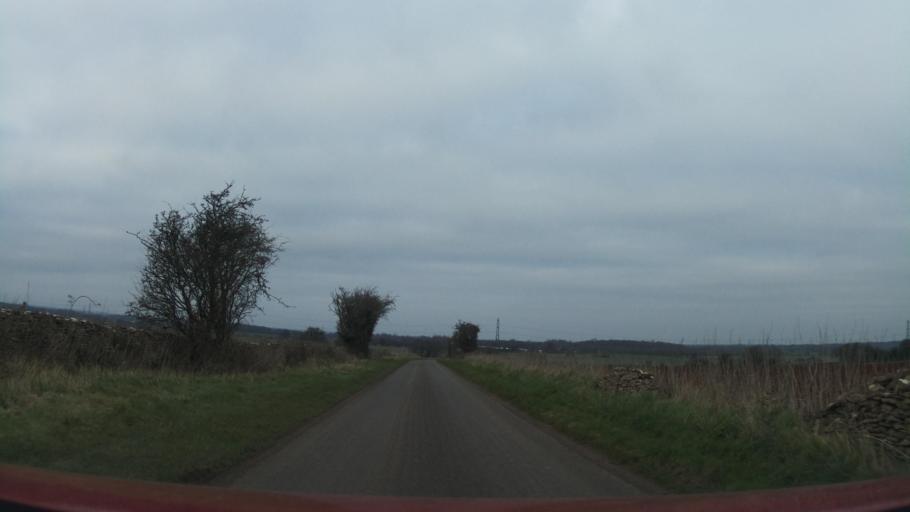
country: GB
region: England
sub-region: Wiltshire
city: Nettleton
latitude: 51.4828
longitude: -2.2840
